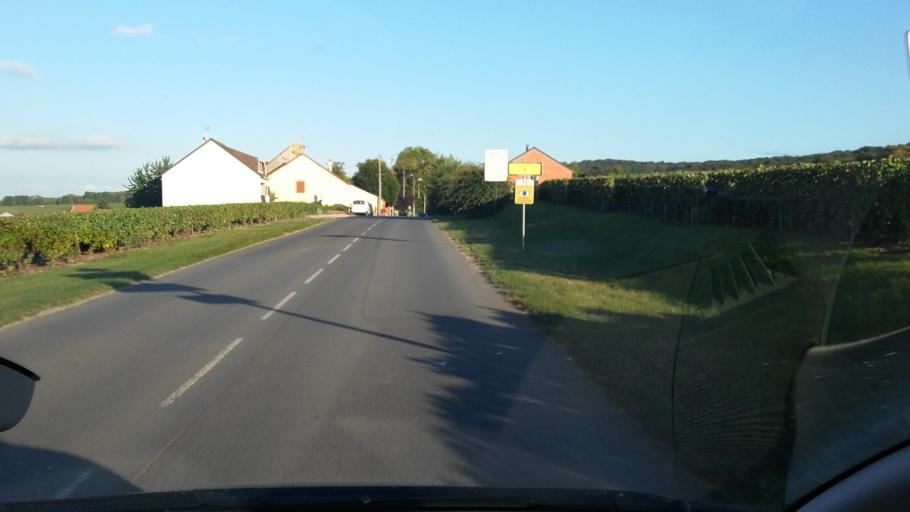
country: FR
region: Champagne-Ardenne
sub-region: Departement de la Marne
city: Rilly-la-Montagne
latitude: 49.1561
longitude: 4.0744
